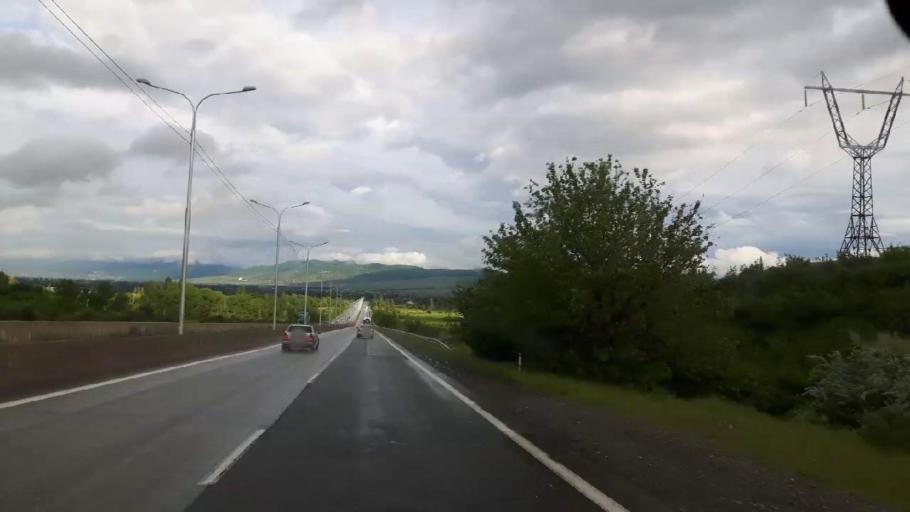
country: GE
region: Shida Kartli
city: Kaspi
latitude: 41.9270
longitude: 44.5343
